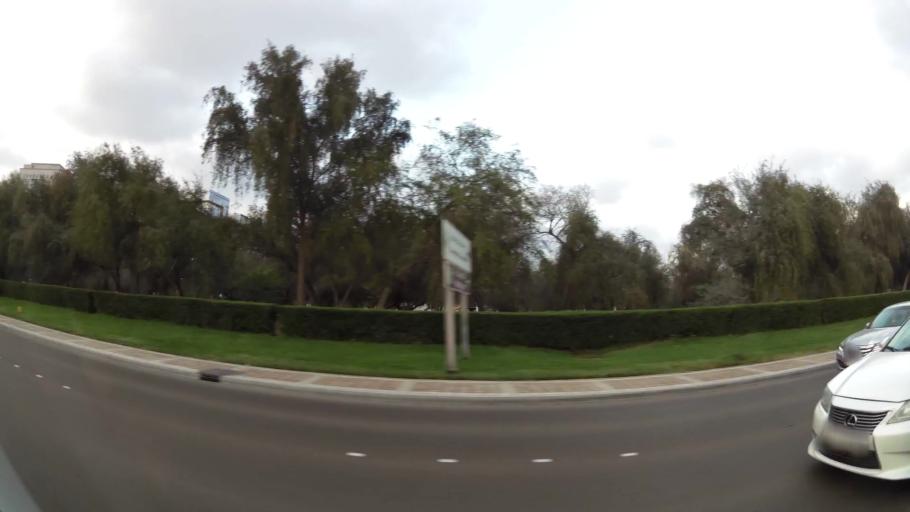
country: AE
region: Abu Dhabi
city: Abu Dhabi
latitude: 24.4272
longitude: 54.4388
